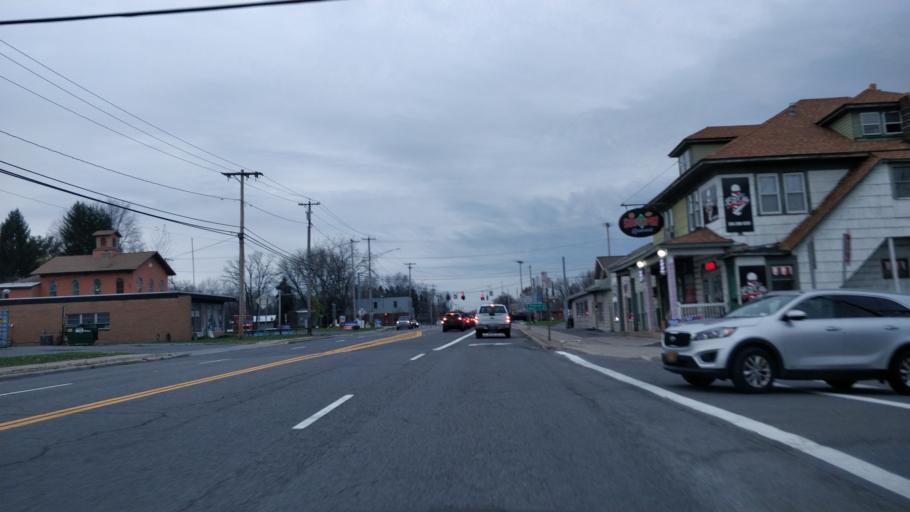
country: US
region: New York
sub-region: Onondaga County
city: North Syracuse
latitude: 43.1740
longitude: -76.1185
